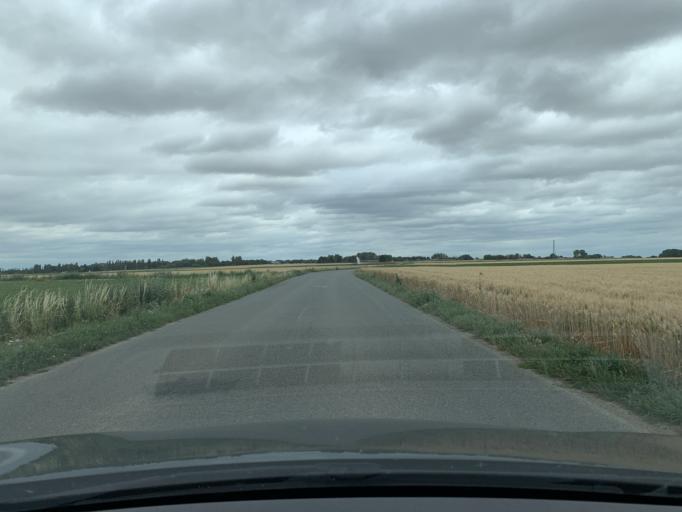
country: FR
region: Nord-Pas-de-Calais
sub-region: Departement du Nord
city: Raillencourt-Sainte-Olle
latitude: 50.2002
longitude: 3.1394
